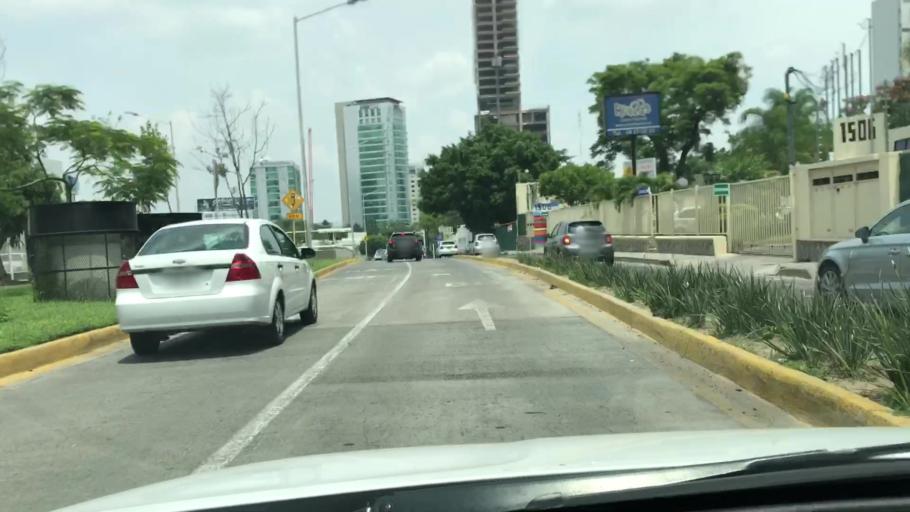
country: MX
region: Jalisco
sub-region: Zapopan
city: Zapopan
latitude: 20.6980
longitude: -103.3739
